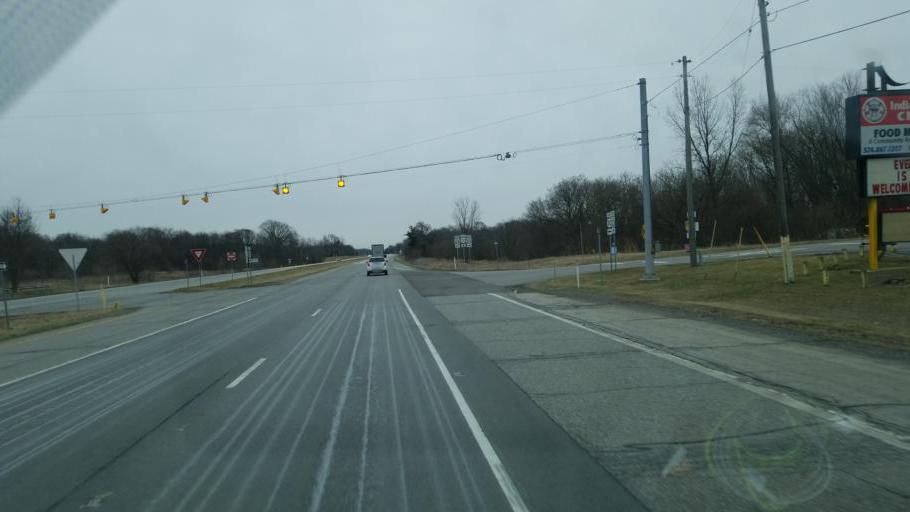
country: US
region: Indiana
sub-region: Starke County
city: Koontz Lake
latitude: 41.3715
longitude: -86.5079
